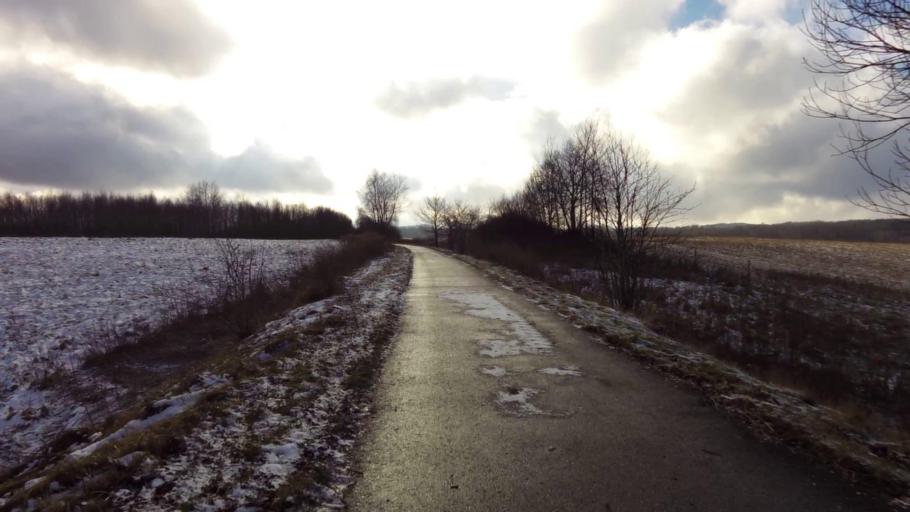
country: PL
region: West Pomeranian Voivodeship
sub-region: Powiat swidwinski
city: Polczyn-Zdroj
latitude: 53.7682
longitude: 16.0699
